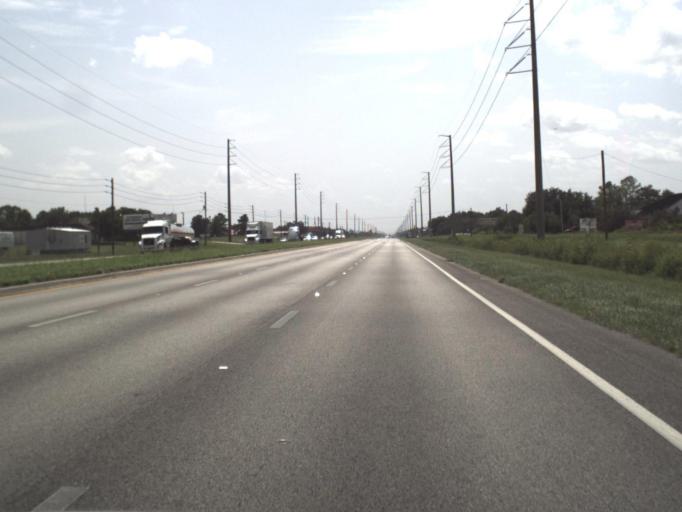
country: US
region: Florida
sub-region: Highlands County
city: Avon Park
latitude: 27.5509
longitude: -81.5084
